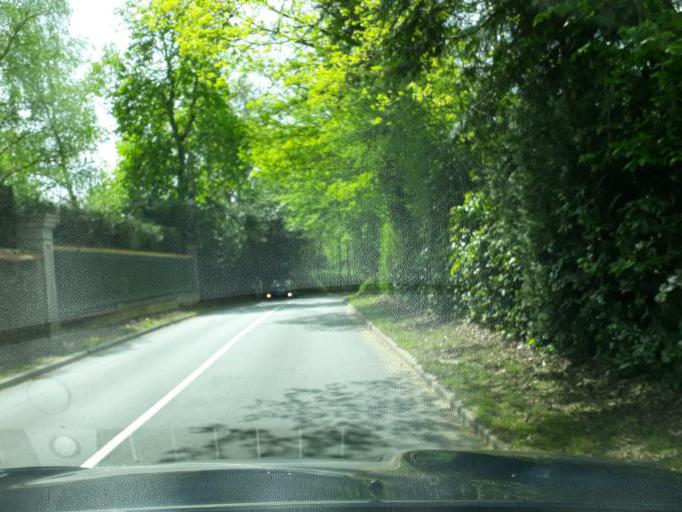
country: FR
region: Ile-de-France
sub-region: Departement des Yvelines
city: Saint-Leger-en-Yvelines
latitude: 48.7276
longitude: 1.7665
